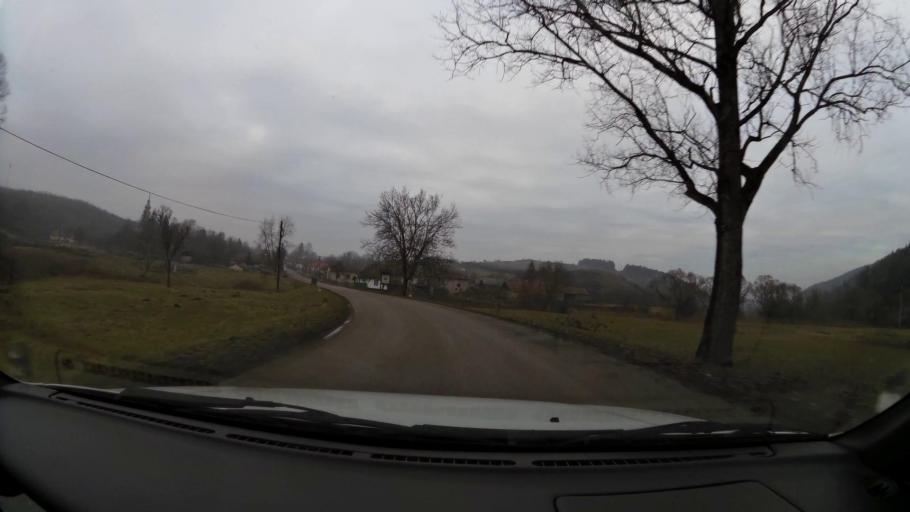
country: HU
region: Borsod-Abauj-Zemplen
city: Rudabanya
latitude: 48.4074
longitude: 20.6582
